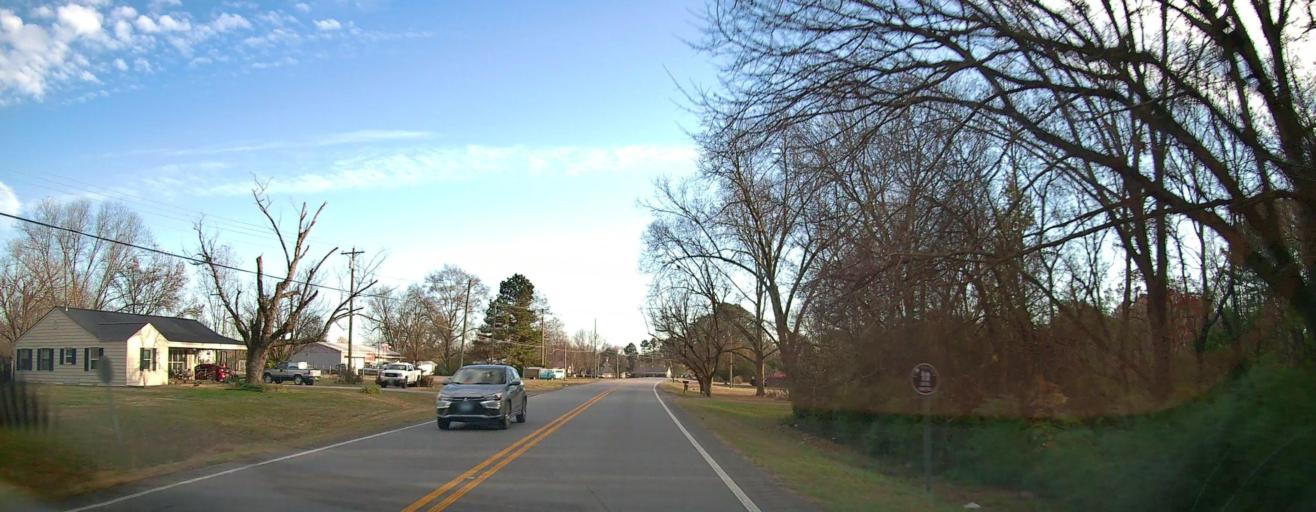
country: US
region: Alabama
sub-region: Marshall County
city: Arab
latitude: 34.3106
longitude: -86.5981
